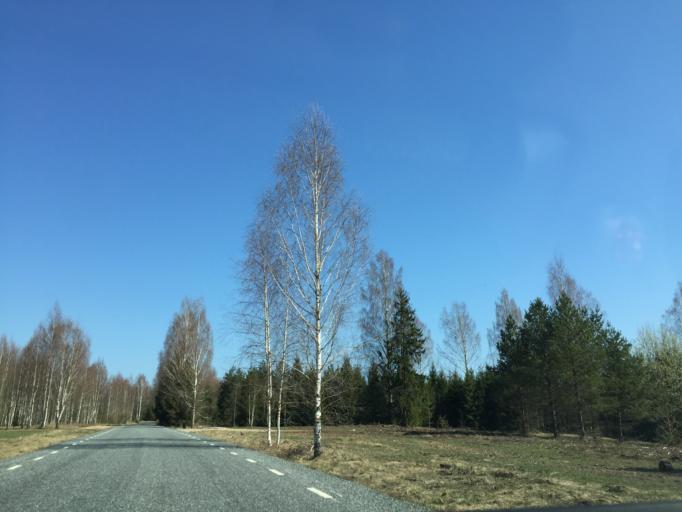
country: EE
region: Tartu
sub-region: Alatskivi vald
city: Kallaste
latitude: 58.5891
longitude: 27.0615
